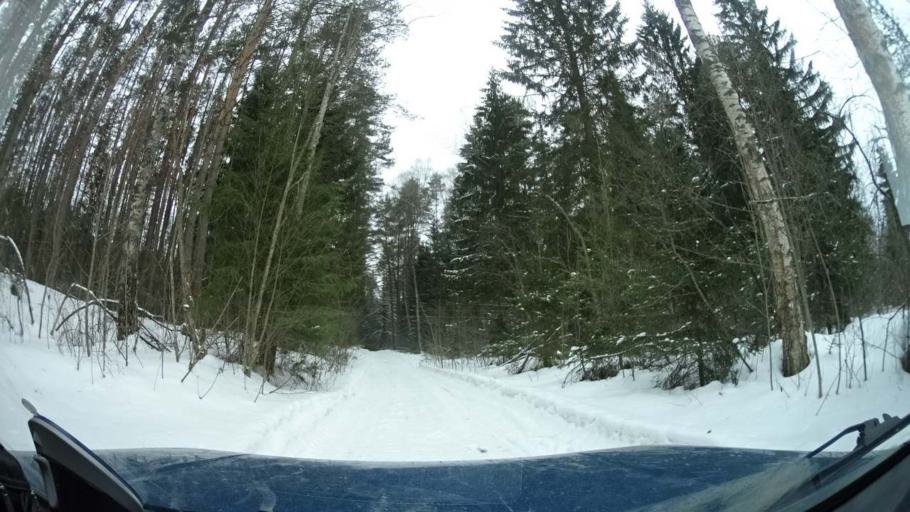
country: RU
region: Tverskaya
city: Radchenko
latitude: 56.6998
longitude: 36.4273
